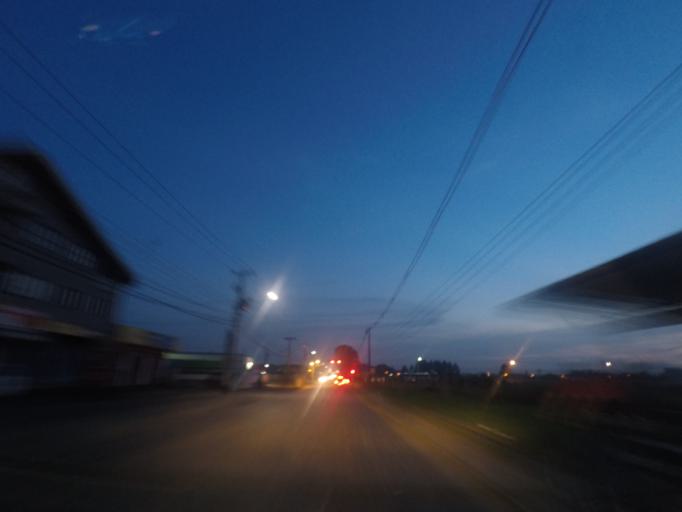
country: BR
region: Parana
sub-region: Pinhais
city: Pinhais
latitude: -25.4874
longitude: -49.1551
